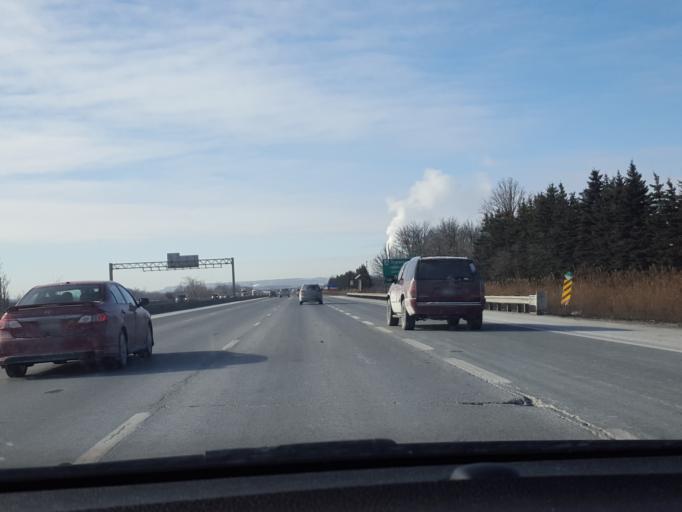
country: CA
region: Ontario
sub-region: Halton
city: Milton
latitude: 43.5822
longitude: -79.8173
